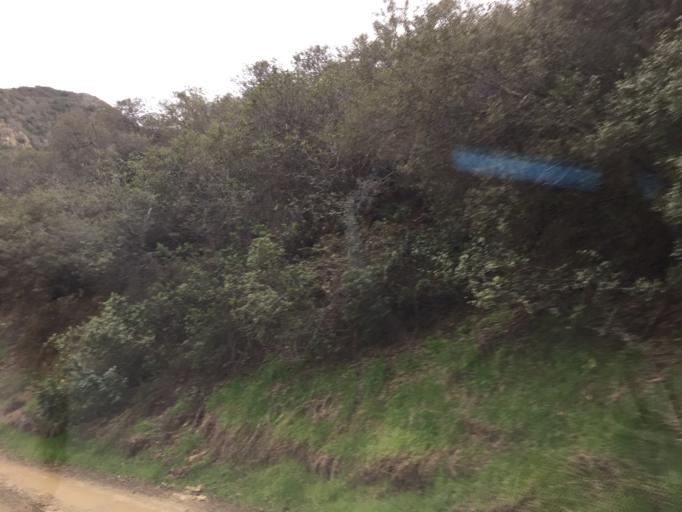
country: US
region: California
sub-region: San Bernardino County
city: Yucaipa
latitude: 34.1165
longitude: -117.0574
